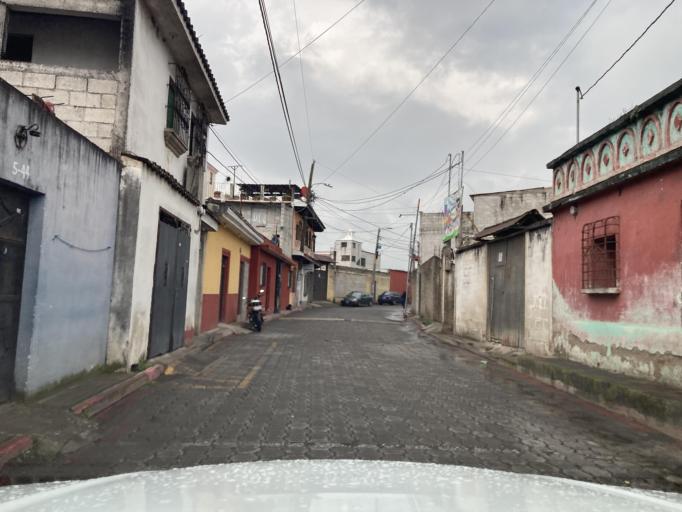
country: GT
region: Sacatepequez
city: San Miguel Duenas
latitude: 14.5232
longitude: -90.7945
